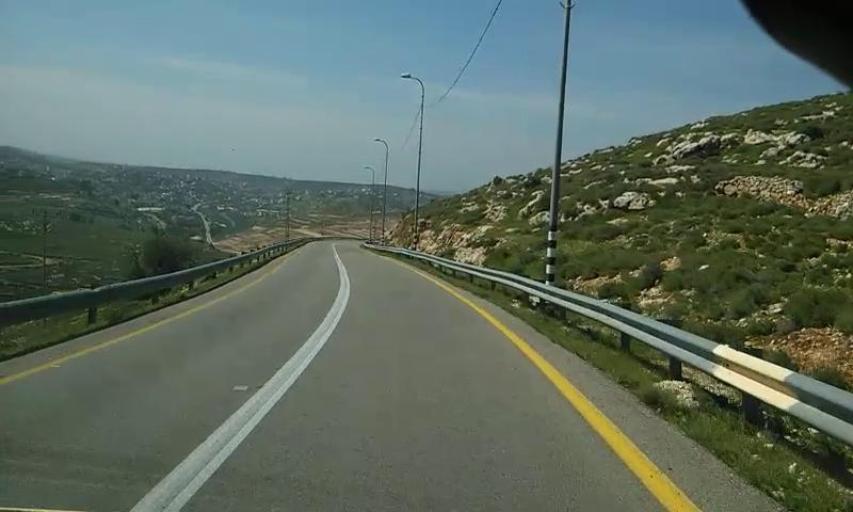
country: PS
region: West Bank
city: Surif
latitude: 31.6699
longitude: 35.0779
